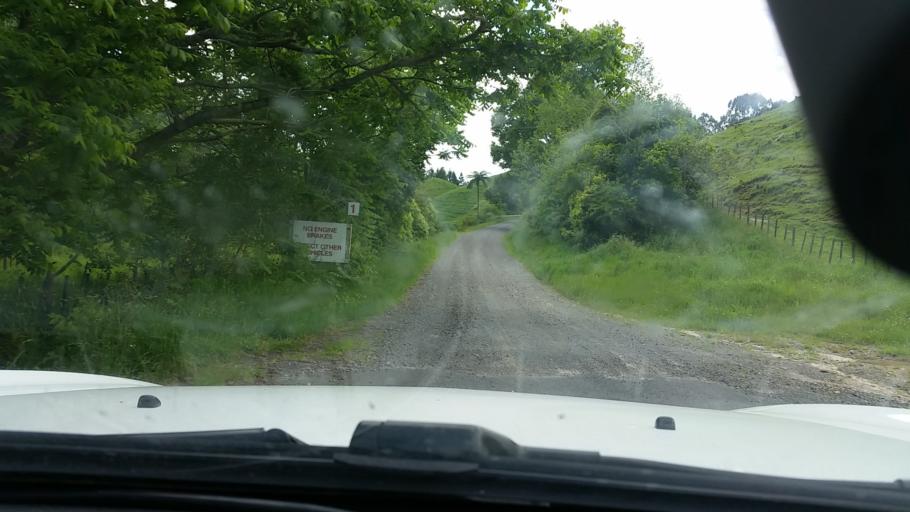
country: NZ
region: Bay of Plenty
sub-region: Rotorua District
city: Rotorua
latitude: -37.9865
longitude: 176.3961
